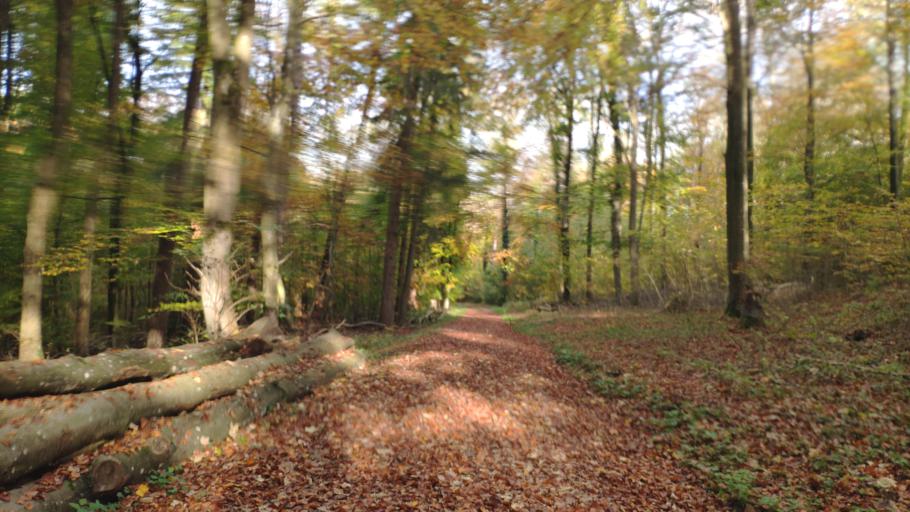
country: DE
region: Baden-Wuerttemberg
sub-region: Tuebingen Region
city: Erbach
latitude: 48.3816
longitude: 9.9254
